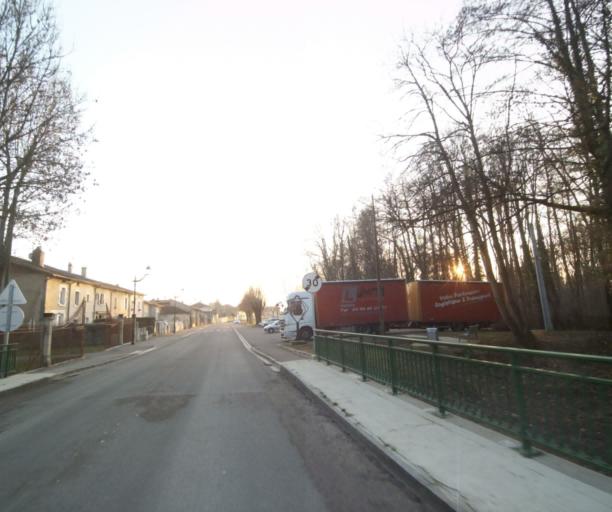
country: FR
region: Champagne-Ardenne
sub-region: Departement de la Haute-Marne
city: Bienville
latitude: 48.6098
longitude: 5.0462
